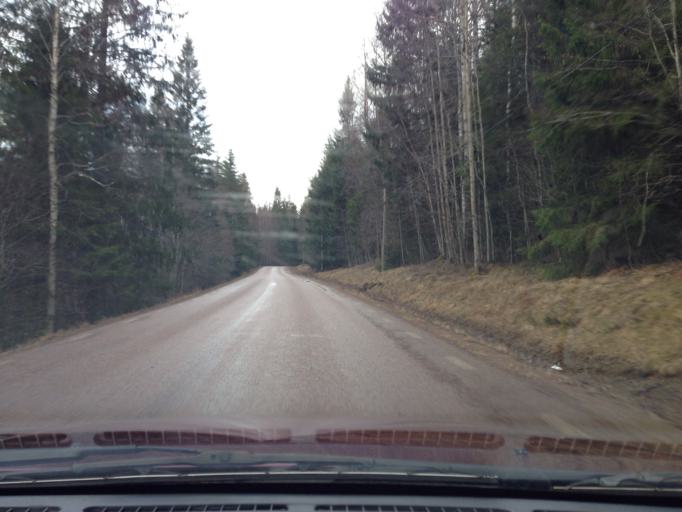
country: SE
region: Dalarna
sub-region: Ludvika Kommun
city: Ludvika
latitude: 60.1667
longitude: 15.2559
